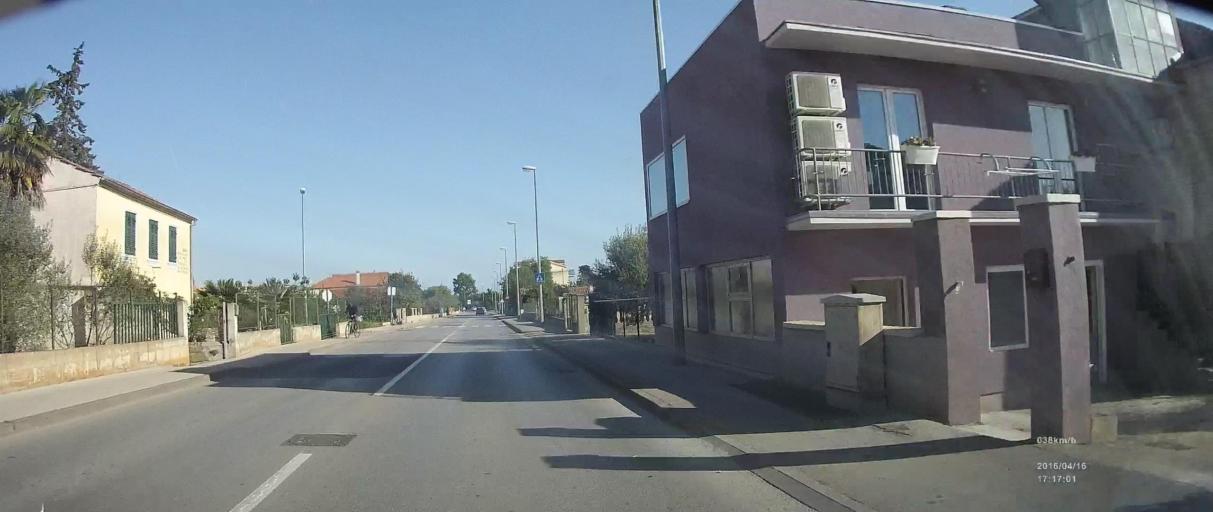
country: HR
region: Zadarska
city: Zadar
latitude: 44.1052
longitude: 15.2445
